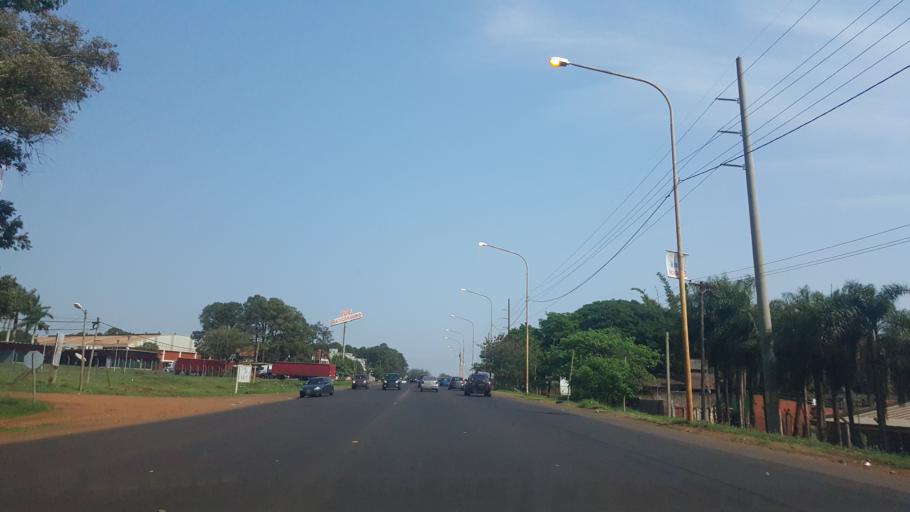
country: AR
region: Misiones
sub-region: Departamento de Capital
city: Posadas
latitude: -27.4017
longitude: -55.9266
